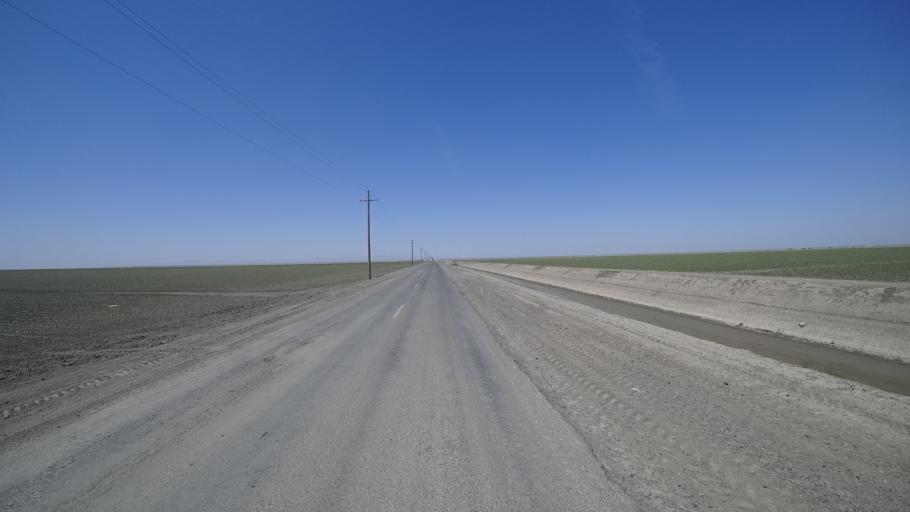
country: US
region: California
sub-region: Kings County
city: Corcoran
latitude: 36.0214
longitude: -119.6584
